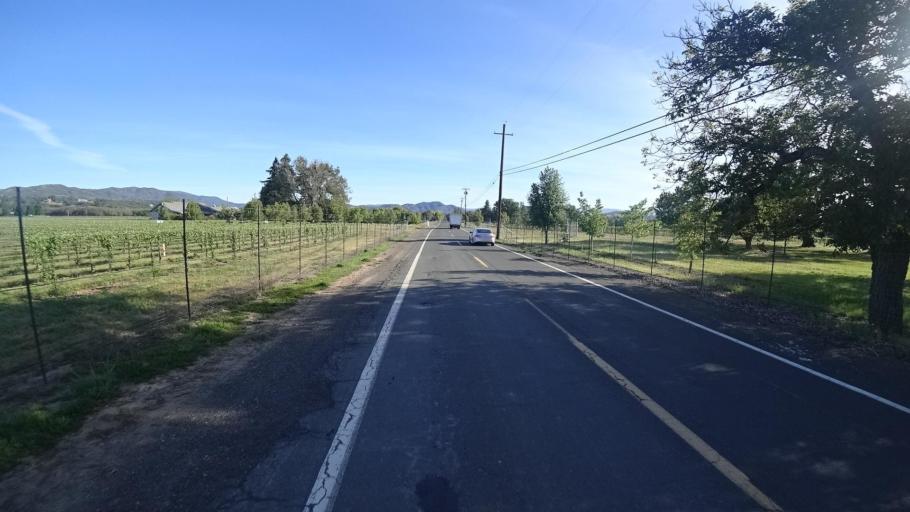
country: US
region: California
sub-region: Lake County
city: Lakeport
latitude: 39.0684
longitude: -122.9498
